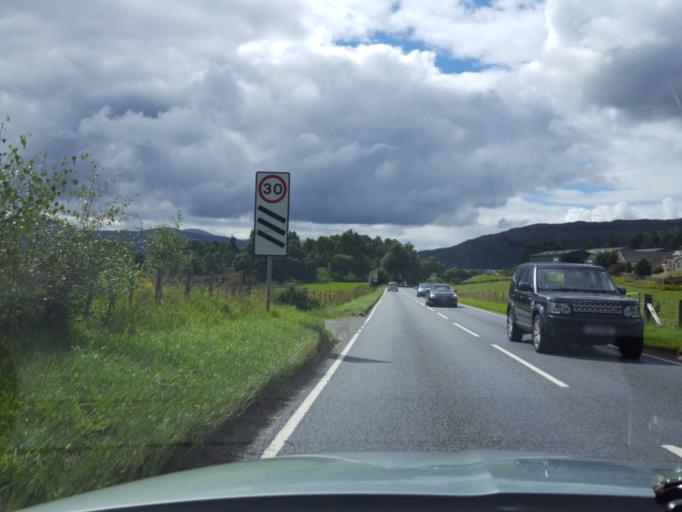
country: GB
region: Scotland
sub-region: Highland
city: Aviemore
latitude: 57.2092
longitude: -3.8243
